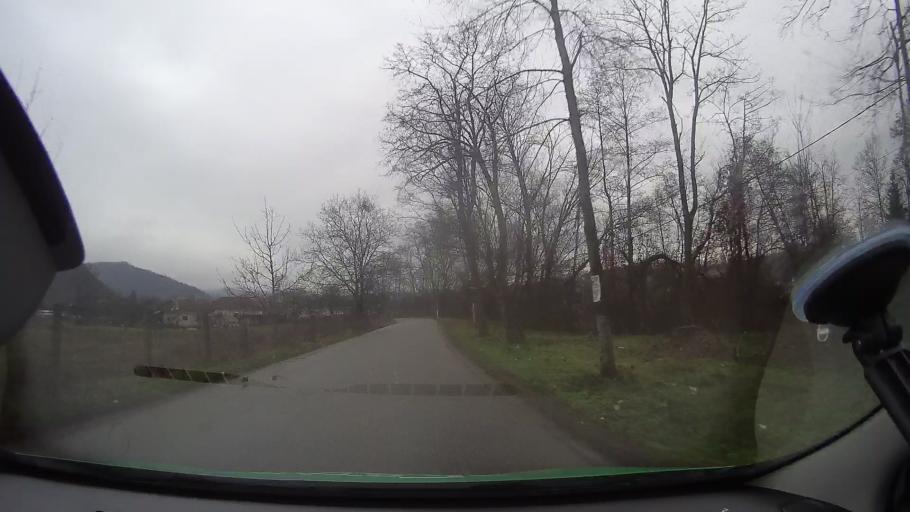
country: RO
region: Arad
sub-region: Comuna Halmagel
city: Halmagel
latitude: 46.2703
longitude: 22.6126
